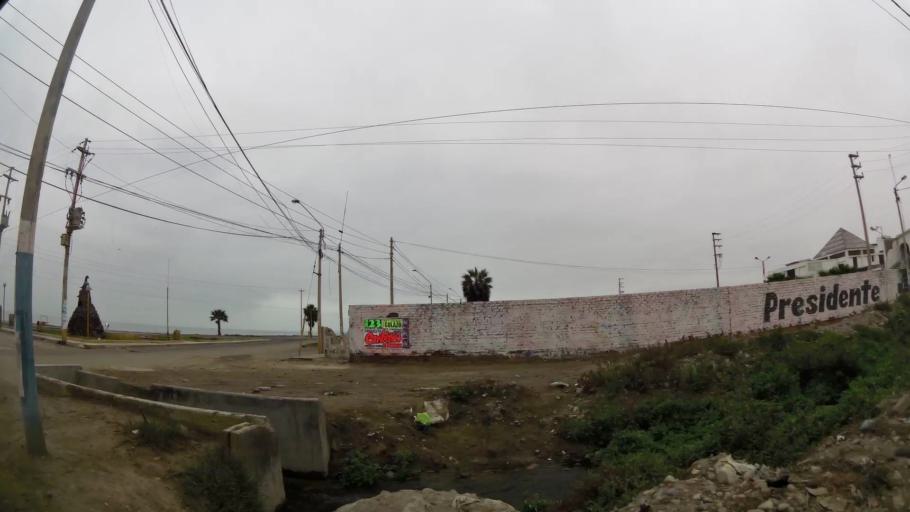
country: PE
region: Ica
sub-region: Provincia de Pisco
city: Pisco
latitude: -13.7274
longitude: -76.2222
